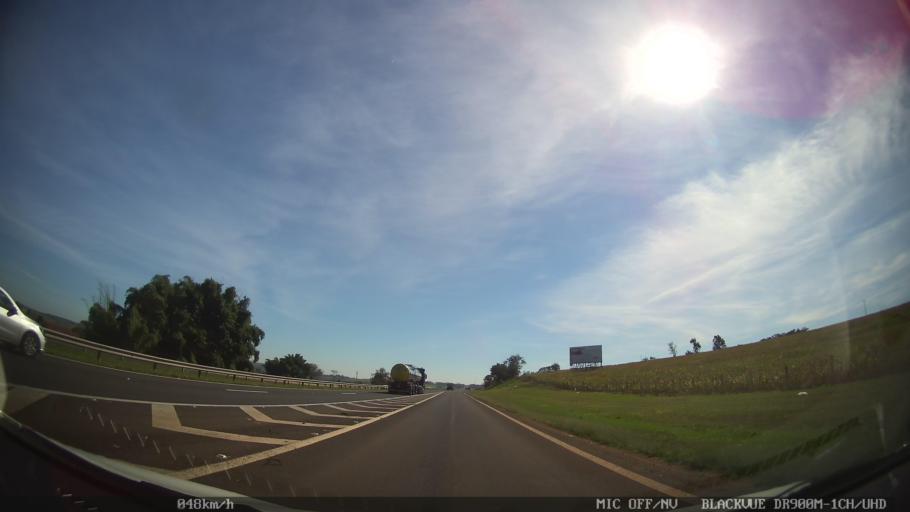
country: BR
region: Sao Paulo
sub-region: Pirassununga
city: Pirassununga
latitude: -22.0719
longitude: -47.4239
